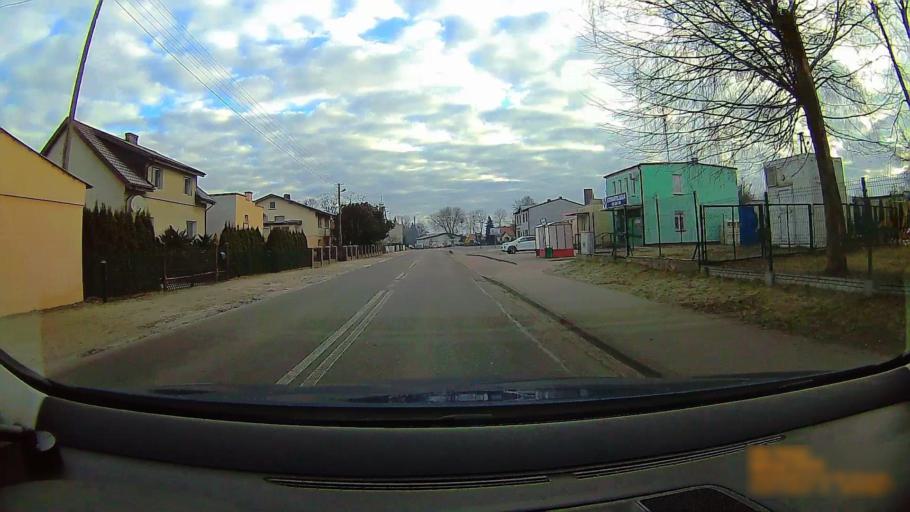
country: PL
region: Greater Poland Voivodeship
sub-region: Powiat koninski
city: Golina
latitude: 52.1958
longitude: 18.1307
